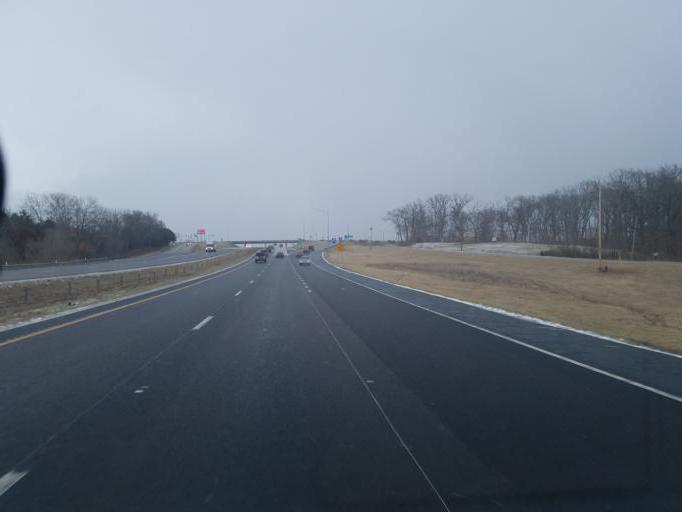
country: US
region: Missouri
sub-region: Boone County
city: Columbia
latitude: 38.9597
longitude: -92.2585
